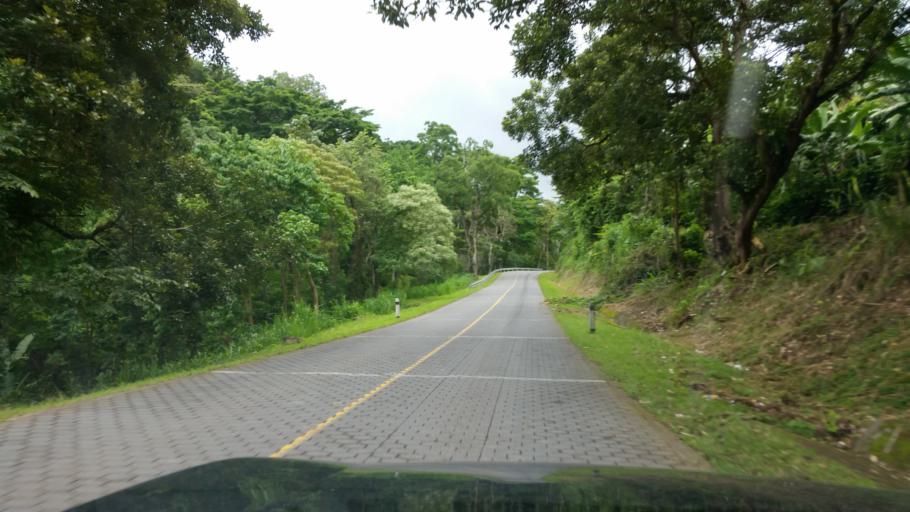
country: NI
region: Jinotega
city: Jinotega
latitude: 13.2016
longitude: -85.7301
